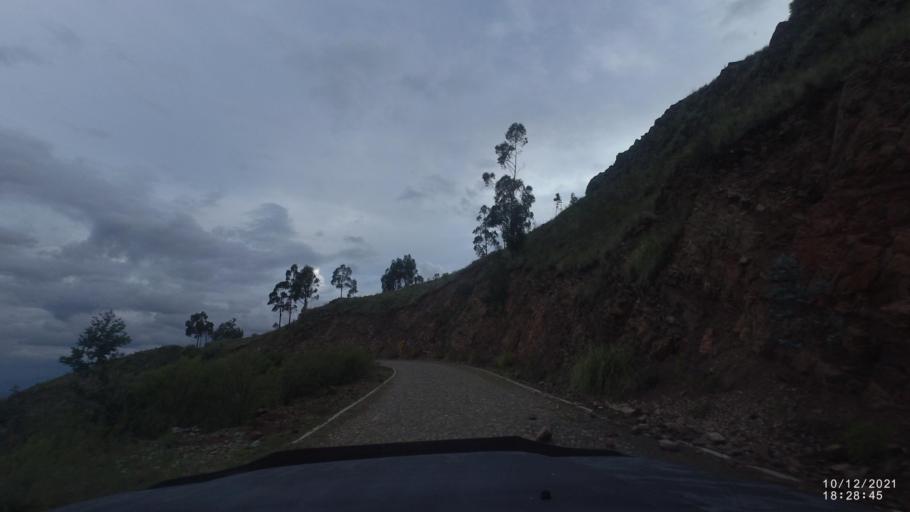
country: BO
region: Cochabamba
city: Tarata
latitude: -17.8102
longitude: -65.9756
